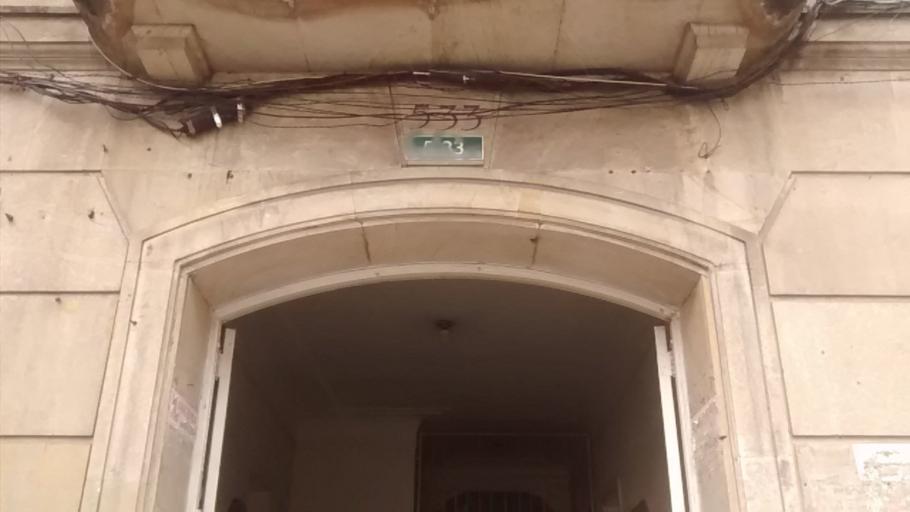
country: CO
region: Bogota D.C.
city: Bogota
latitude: 4.6072
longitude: -74.0694
